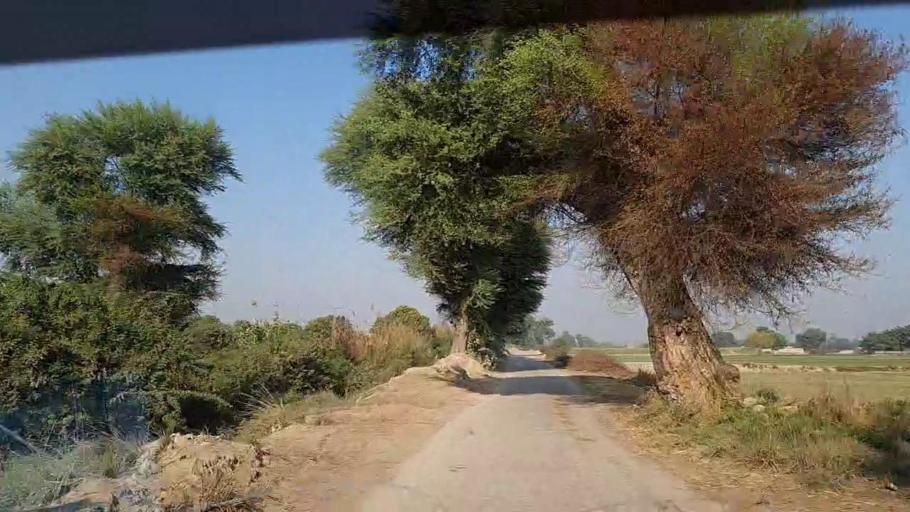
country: PK
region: Sindh
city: Hingorja
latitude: 27.2401
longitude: 68.3208
